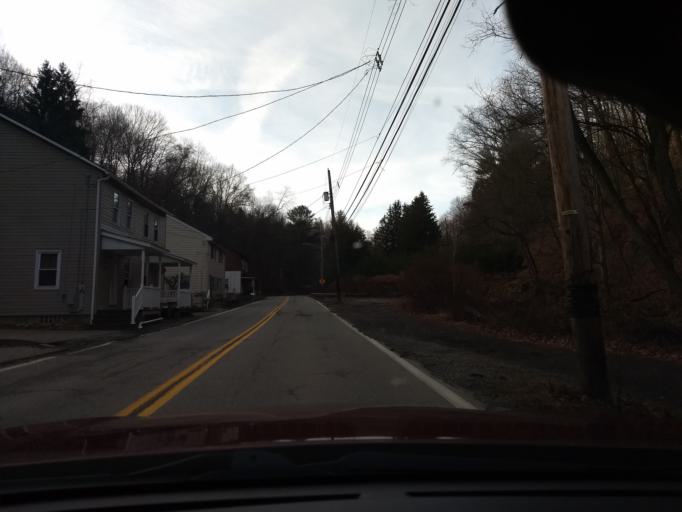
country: US
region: Pennsylvania
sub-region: Allegheny County
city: Brentwood
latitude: 40.3667
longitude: -79.9523
